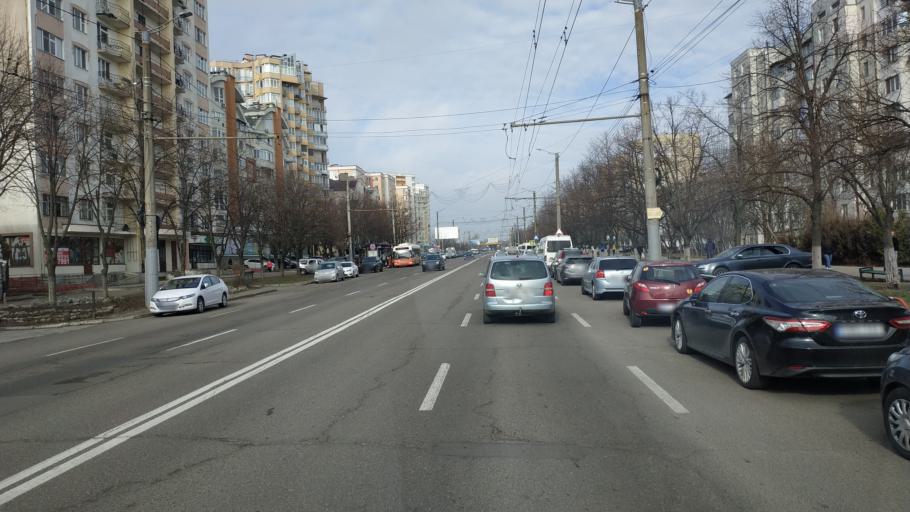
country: MD
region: Chisinau
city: Vatra
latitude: 47.0407
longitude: 28.7653
